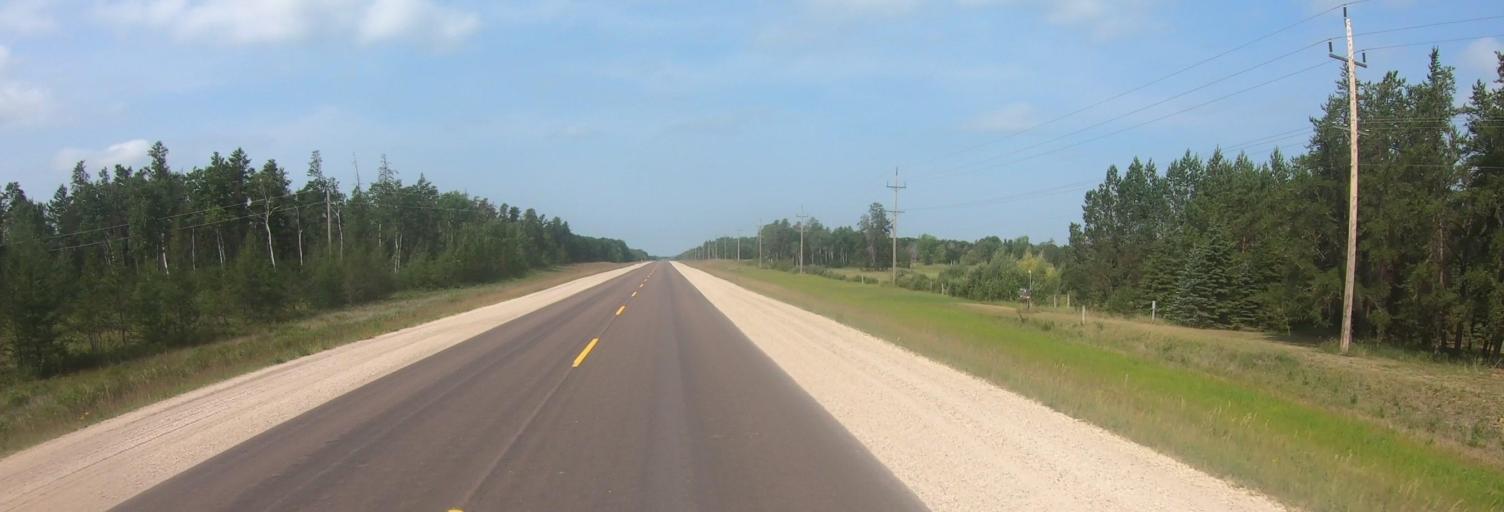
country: CA
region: Manitoba
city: La Broquerie
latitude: 49.2668
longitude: -96.4289
